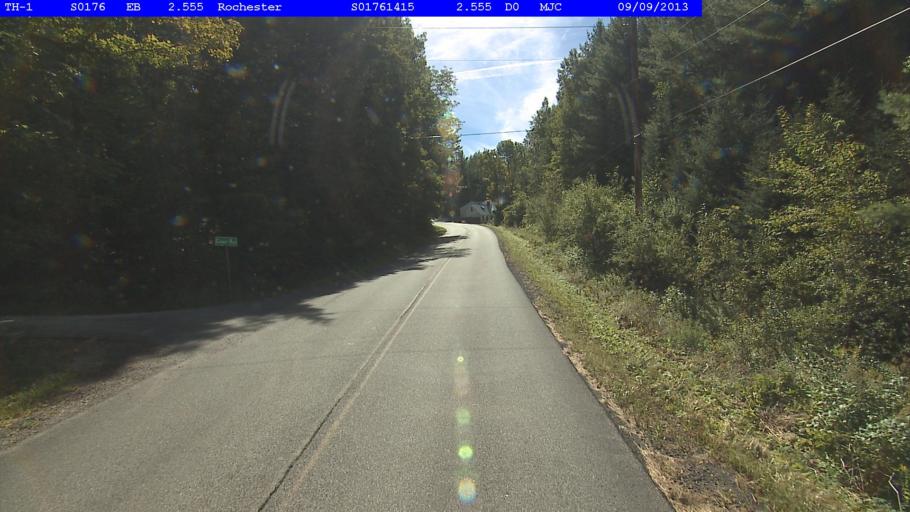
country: US
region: Vermont
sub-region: Orange County
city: Randolph
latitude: 43.8661
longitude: -72.7673
